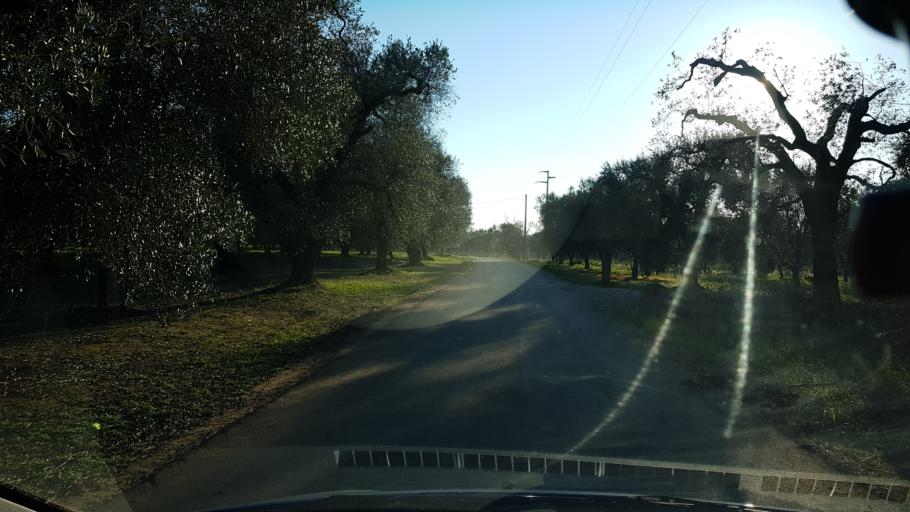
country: IT
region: Apulia
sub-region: Provincia di Brindisi
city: Mesagne
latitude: 40.5759
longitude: 17.8745
